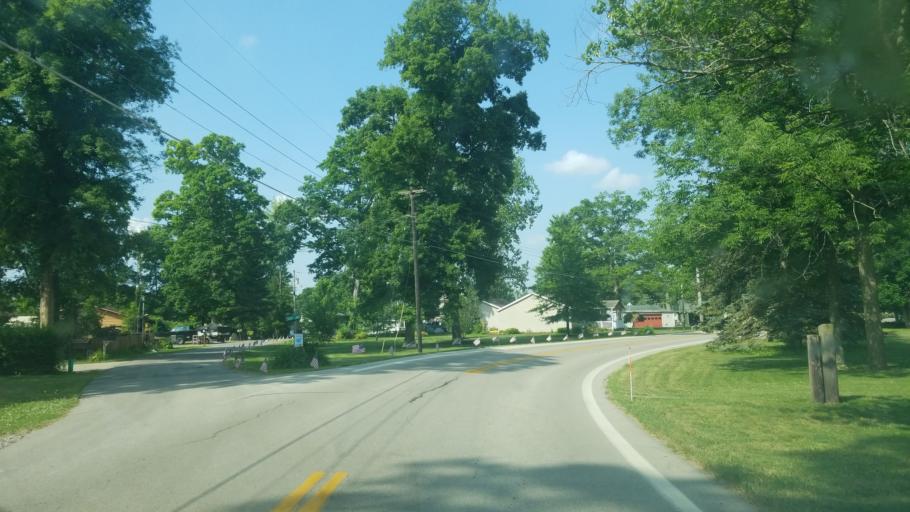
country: US
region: Ohio
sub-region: Logan County
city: Russells Point
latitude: 40.5050
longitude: -83.8506
